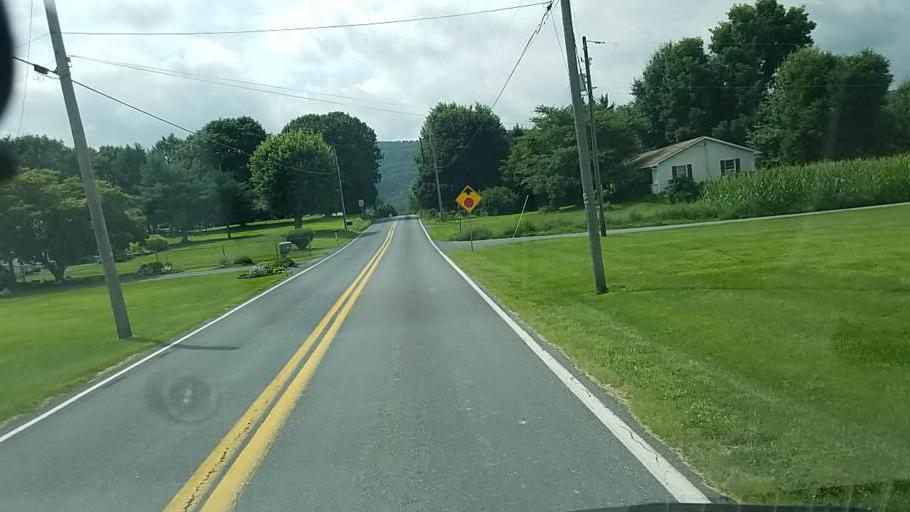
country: US
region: Pennsylvania
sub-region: Dauphin County
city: Millersburg
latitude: 40.5469
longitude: -76.8919
